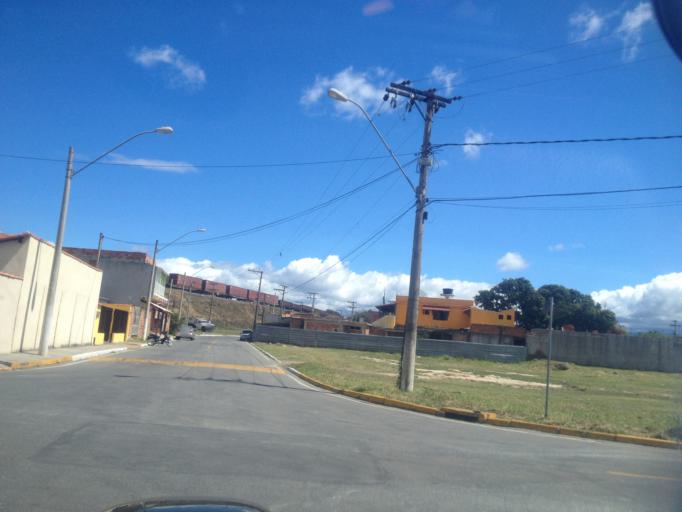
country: BR
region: Rio de Janeiro
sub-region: Porto Real
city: Porto Real
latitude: -22.4465
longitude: -44.3091
